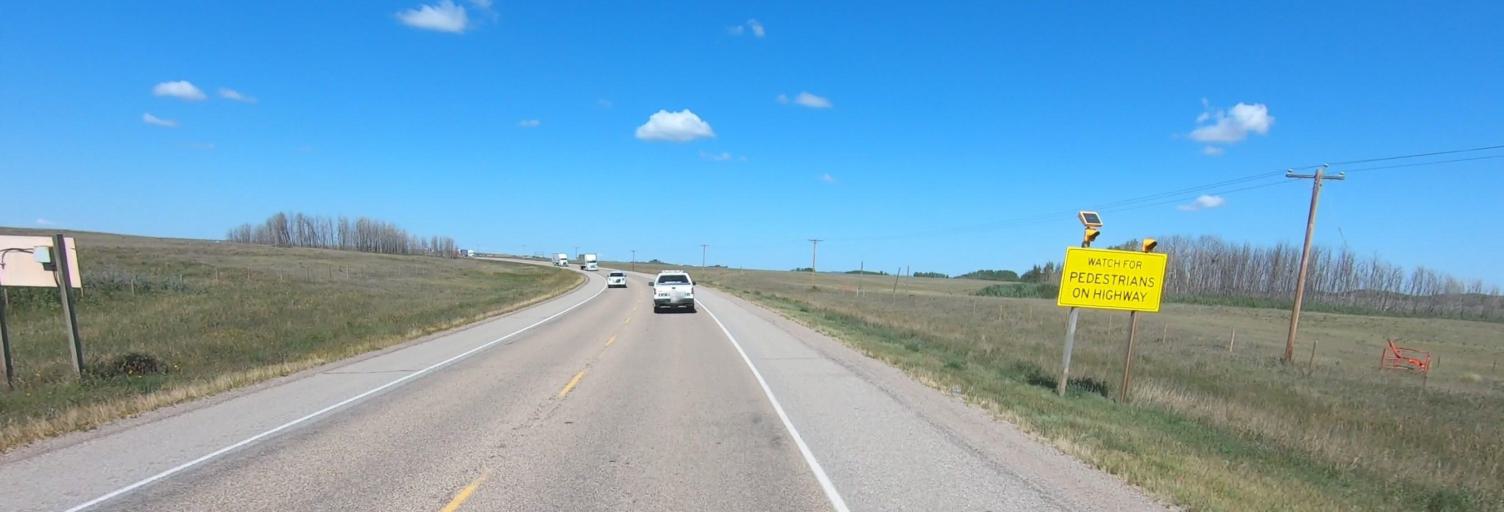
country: CA
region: Alberta
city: Strathmore
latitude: 50.8800
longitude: -113.1697
